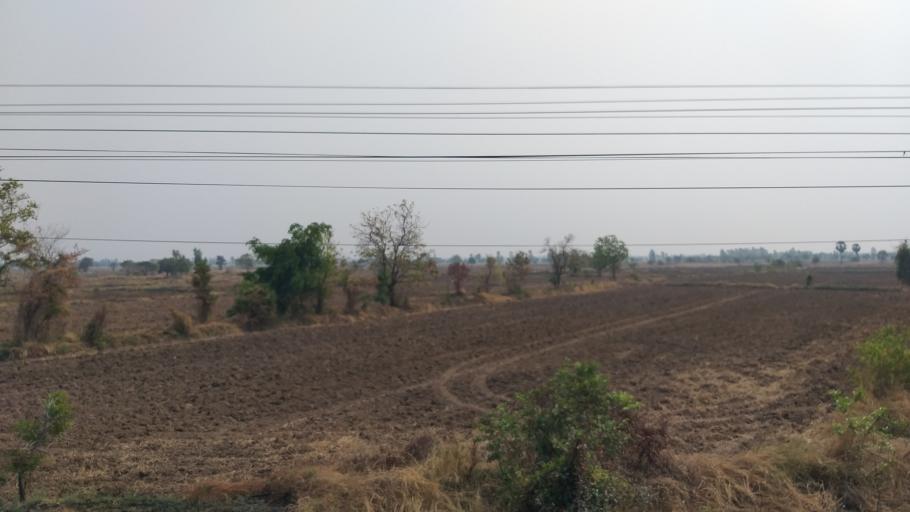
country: TH
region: Nakhon Ratchasima
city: Non Sung
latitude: 15.2181
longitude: 102.3603
